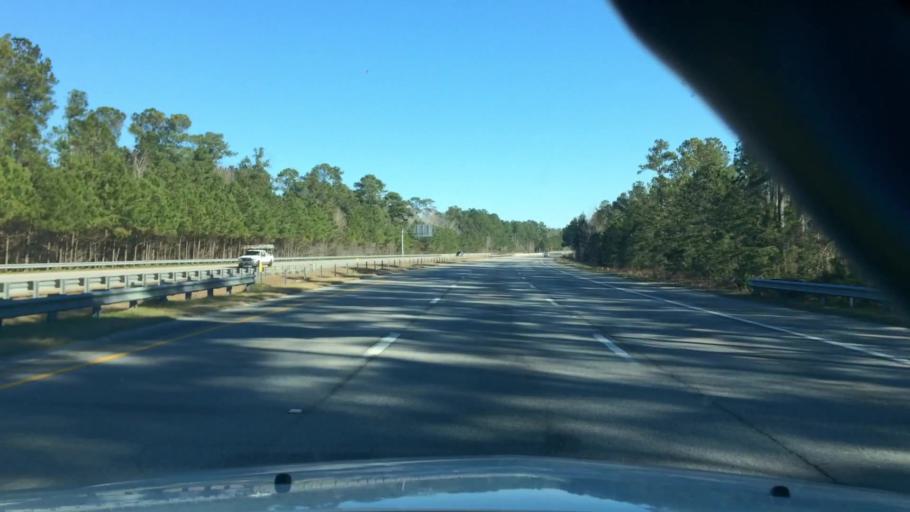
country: US
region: South Carolina
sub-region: Horry County
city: North Myrtle Beach
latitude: 33.8616
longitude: -78.6951
